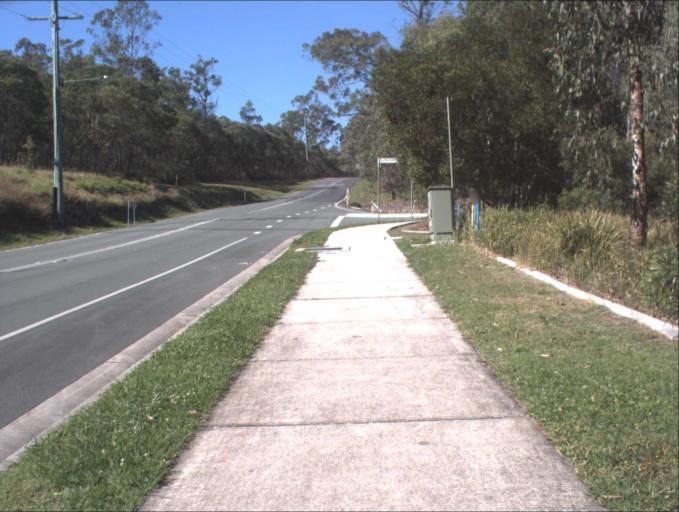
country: AU
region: Queensland
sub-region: Logan
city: Windaroo
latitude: -27.7228
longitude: 153.1737
